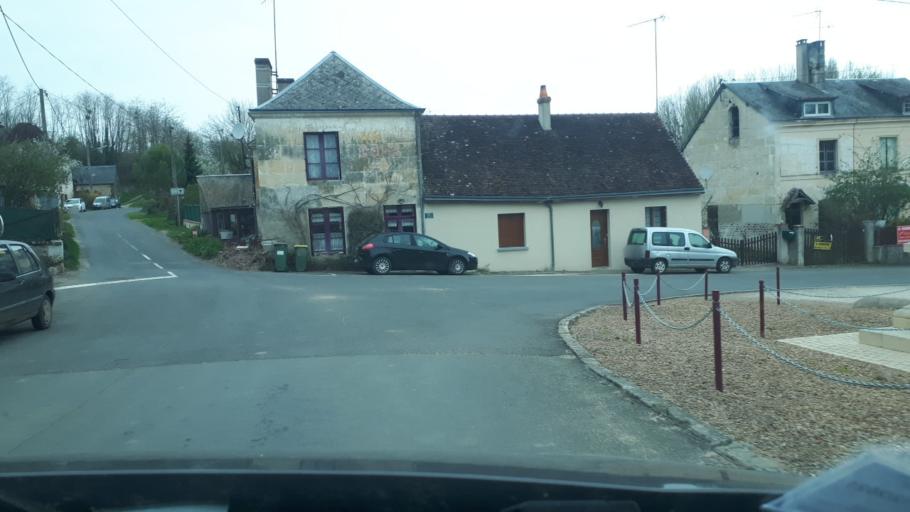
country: FR
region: Centre
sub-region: Departement du Loir-et-Cher
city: Lunay
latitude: 47.7624
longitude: 0.9220
